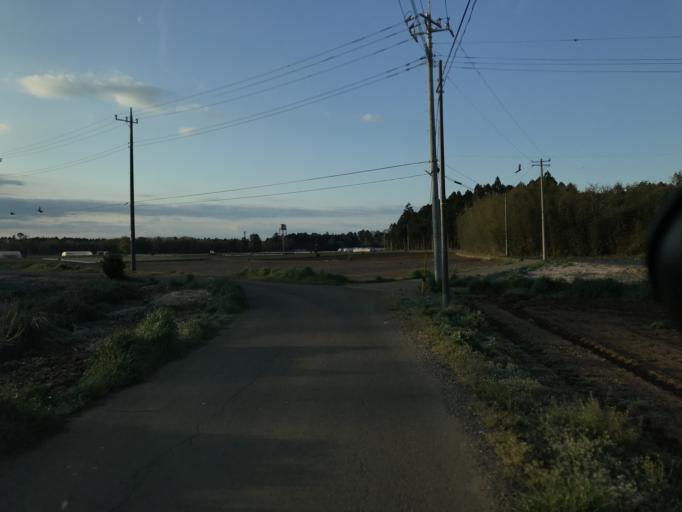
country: JP
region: Chiba
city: Omigawa
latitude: 35.7984
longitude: 140.5418
